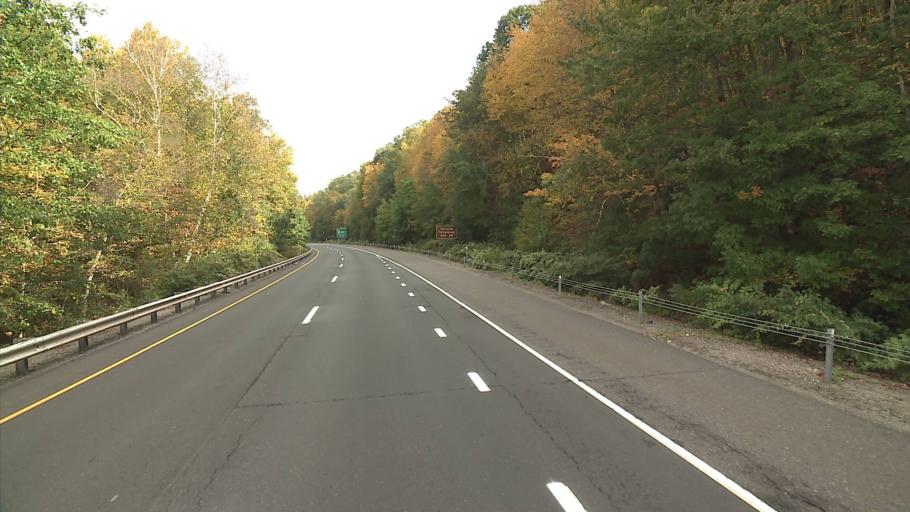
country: US
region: Connecticut
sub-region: Litchfield County
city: Thomaston
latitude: 41.6695
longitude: -73.0694
